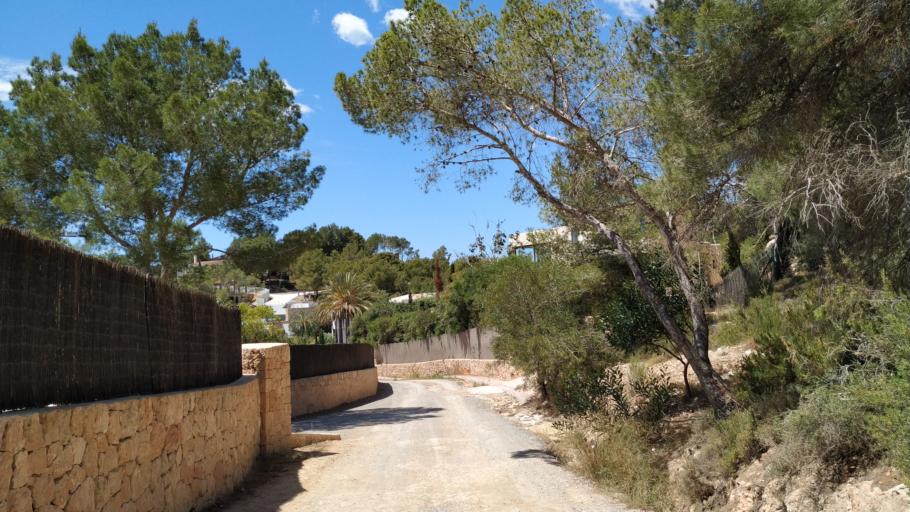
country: ES
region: Balearic Islands
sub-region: Illes Balears
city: Ibiza
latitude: 38.9205
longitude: 1.4737
